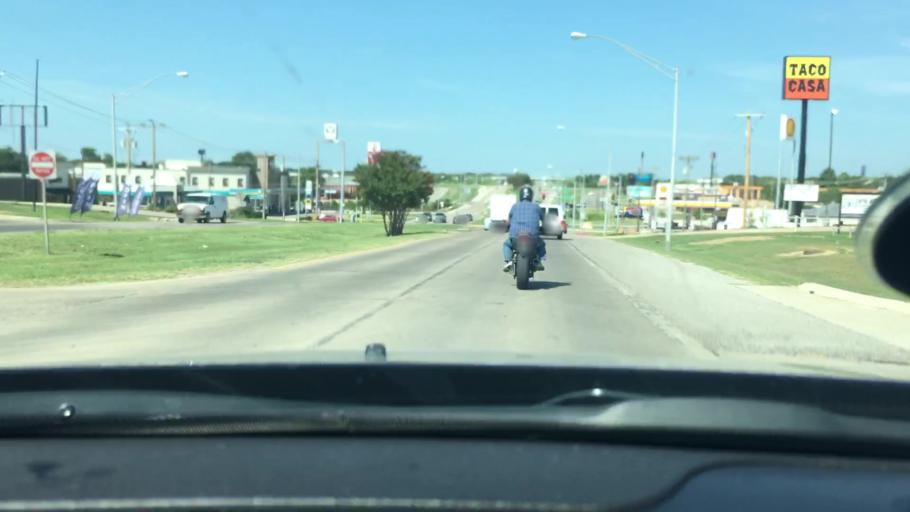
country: US
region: Oklahoma
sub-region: Carter County
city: Ardmore
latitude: 34.1730
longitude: -97.1587
